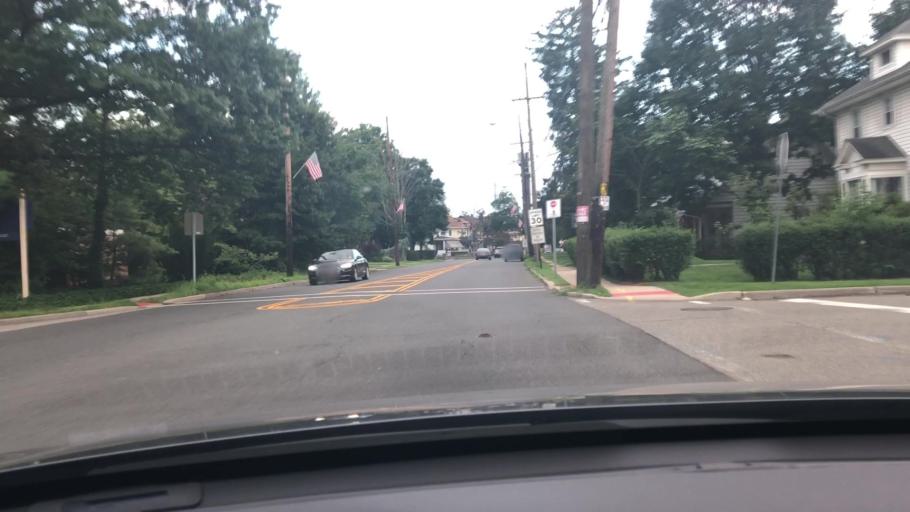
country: US
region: New Jersey
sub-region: Middlesex County
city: Milltown
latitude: 40.4624
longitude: -74.4465
